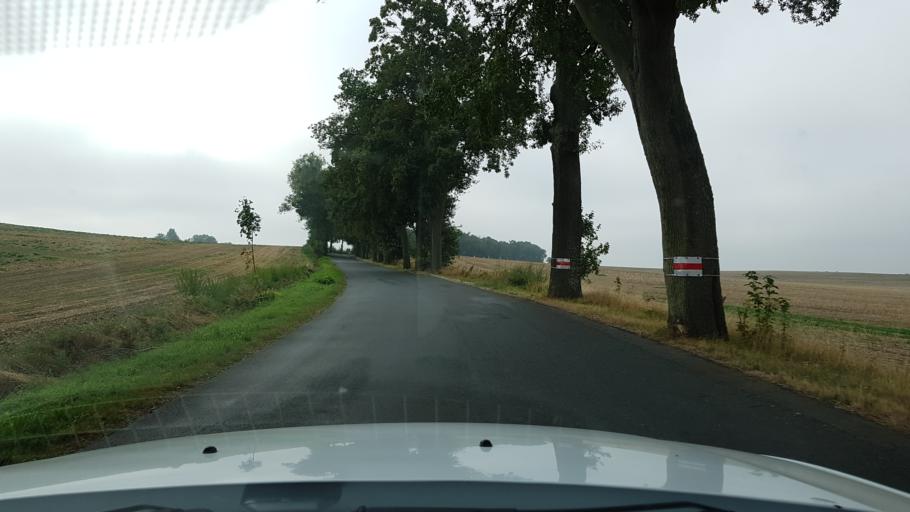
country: PL
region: West Pomeranian Voivodeship
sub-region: Powiat gryfinski
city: Moryn
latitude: 52.8860
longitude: 14.3777
